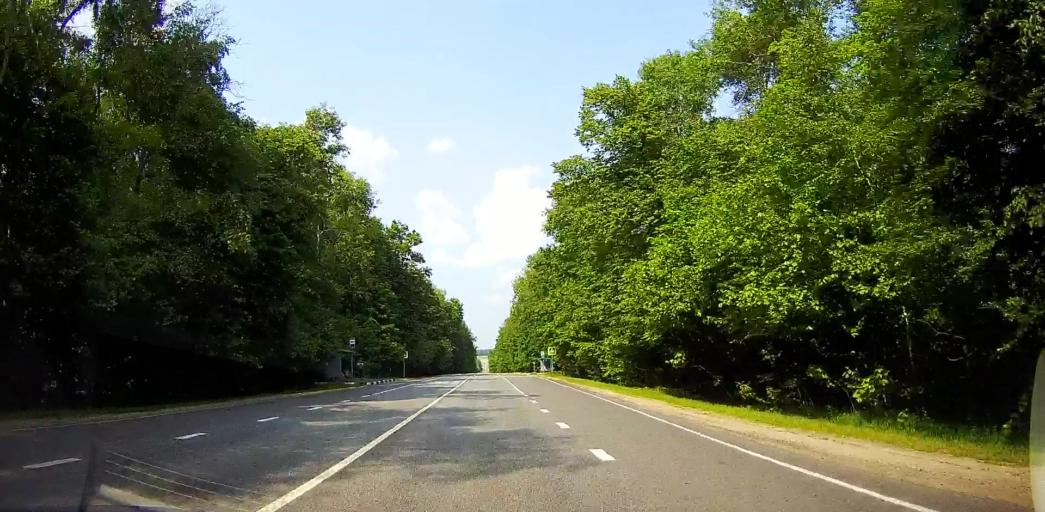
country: RU
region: Moskovskaya
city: Malino
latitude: 55.0107
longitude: 38.1723
